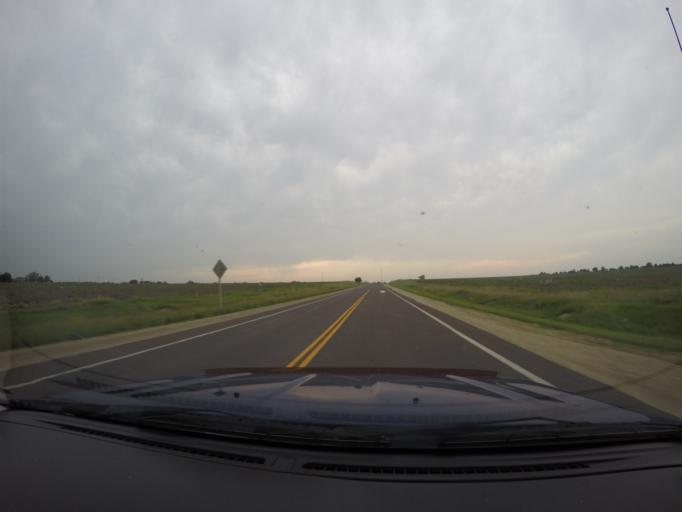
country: US
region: Kansas
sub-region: Riley County
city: Fort Riley North
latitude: 39.3002
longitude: -96.8123
